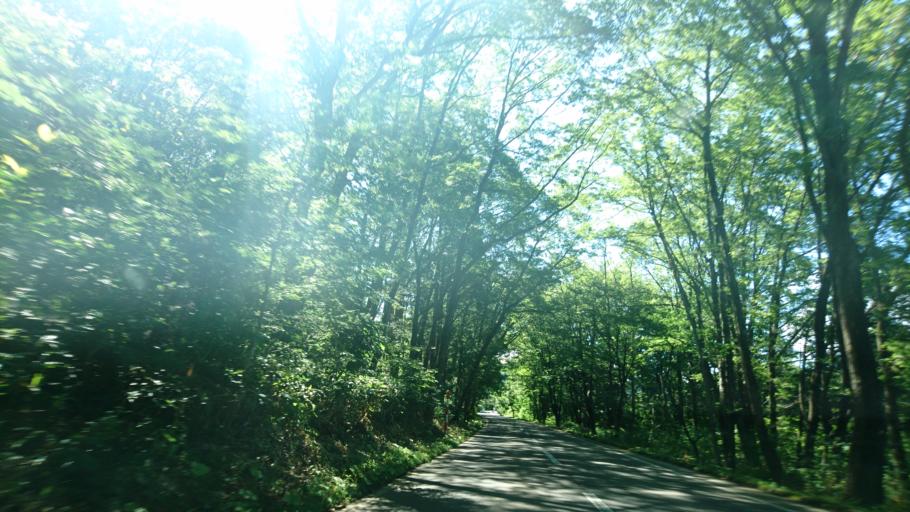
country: JP
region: Akita
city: Kakunodatemachi
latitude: 39.7406
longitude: 140.6896
